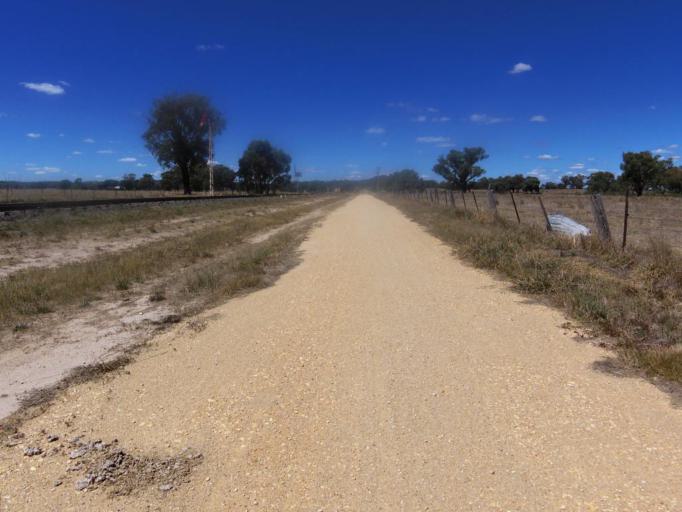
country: AU
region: Victoria
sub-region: Mount Alexander
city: Castlemaine
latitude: -37.0193
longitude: 144.1460
